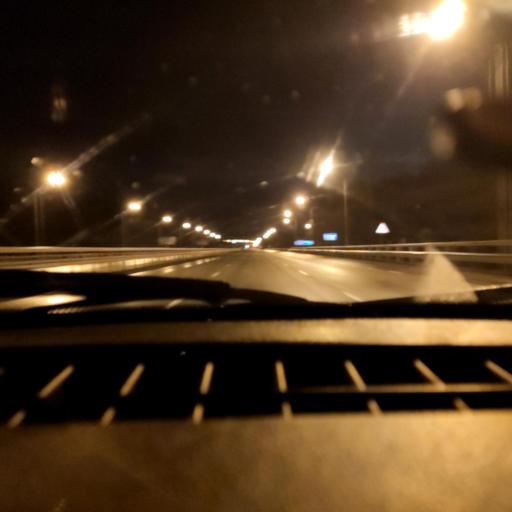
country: RU
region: Bashkortostan
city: Avdon
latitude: 54.6705
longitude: 55.8394
